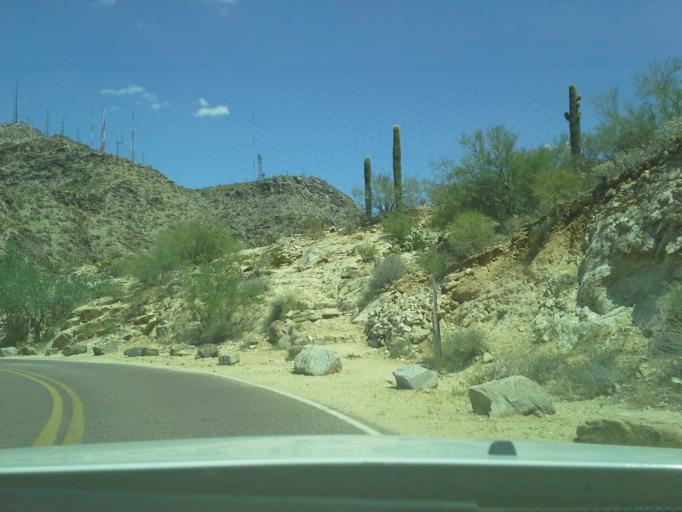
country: US
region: Arizona
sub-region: Maricopa County
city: Laveen
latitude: 33.3281
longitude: -112.0739
